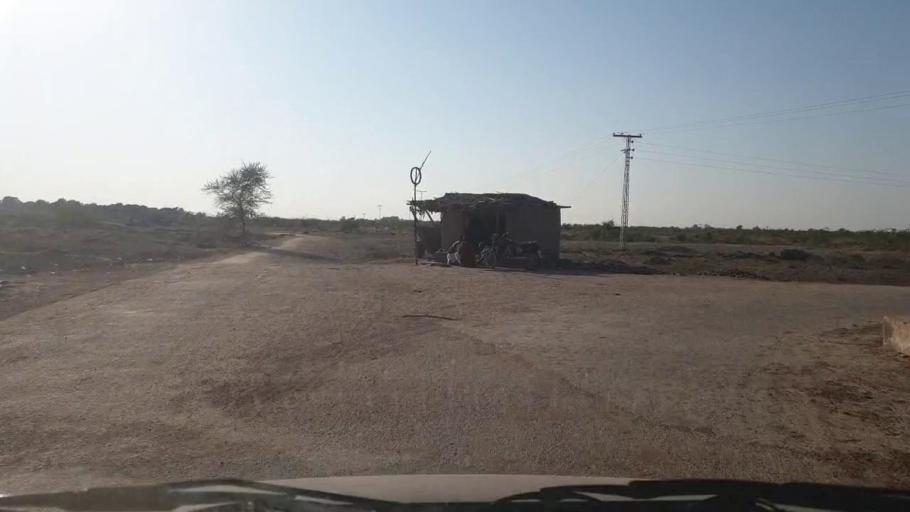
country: PK
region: Sindh
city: Samaro
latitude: 25.3398
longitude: 69.3000
